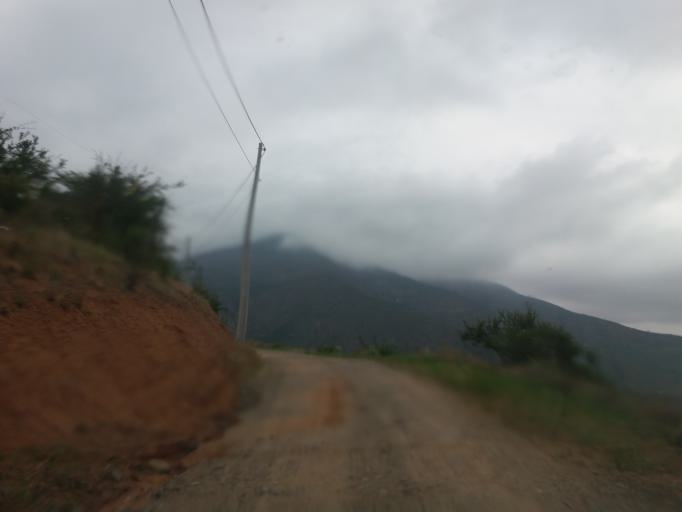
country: CL
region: Valparaiso
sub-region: Provincia de Marga Marga
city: Limache
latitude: -33.0233
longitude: -71.1324
